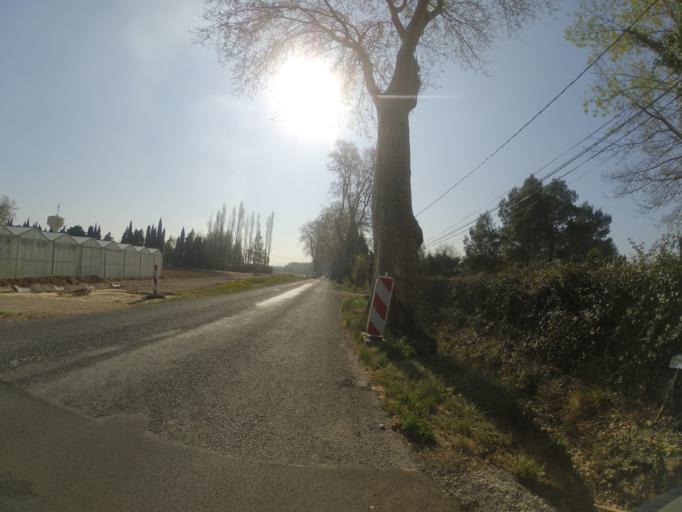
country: FR
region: Languedoc-Roussillon
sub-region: Departement des Pyrenees-Orientales
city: Thuir
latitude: 42.6435
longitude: 2.7411
